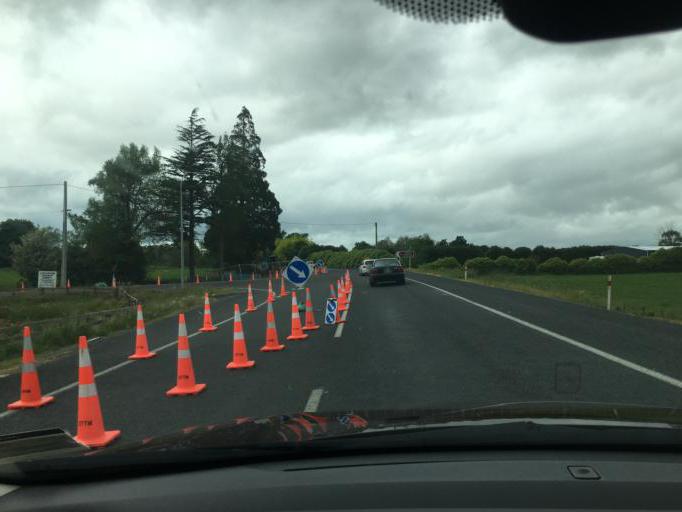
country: NZ
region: Waikato
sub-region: Waipa District
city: Cambridge
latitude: -37.9246
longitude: 175.4342
